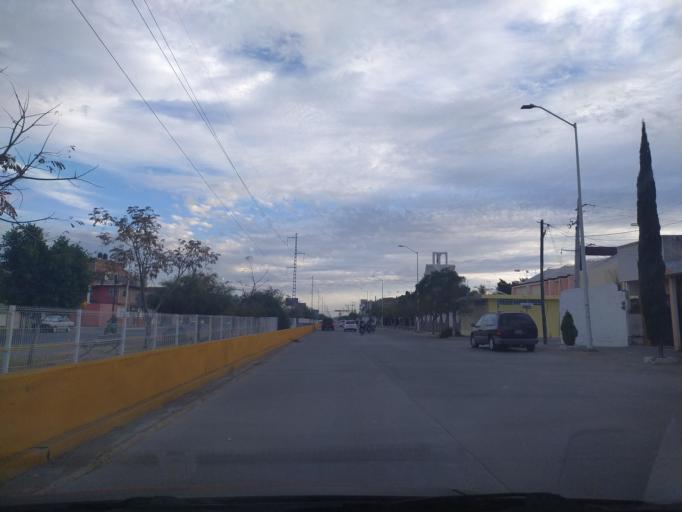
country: LA
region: Oudomxai
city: Muang La
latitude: 21.0267
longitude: 101.8695
